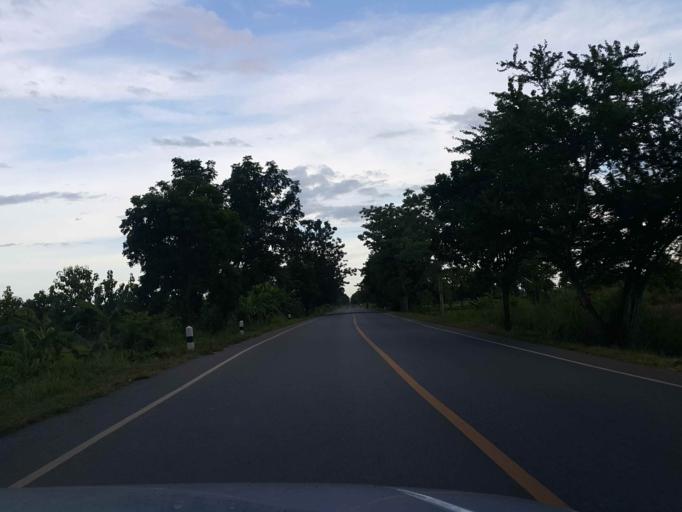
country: TH
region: Sukhothai
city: Sawankhalok
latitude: 17.3702
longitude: 99.7415
